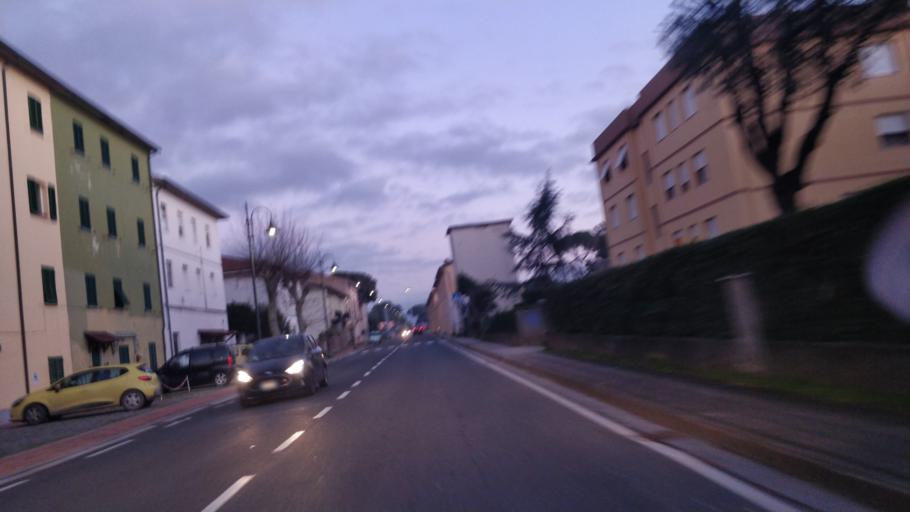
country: IT
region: Tuscany
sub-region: Provincia di Livorno
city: Vada
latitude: 43.3507
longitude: 10.4591
